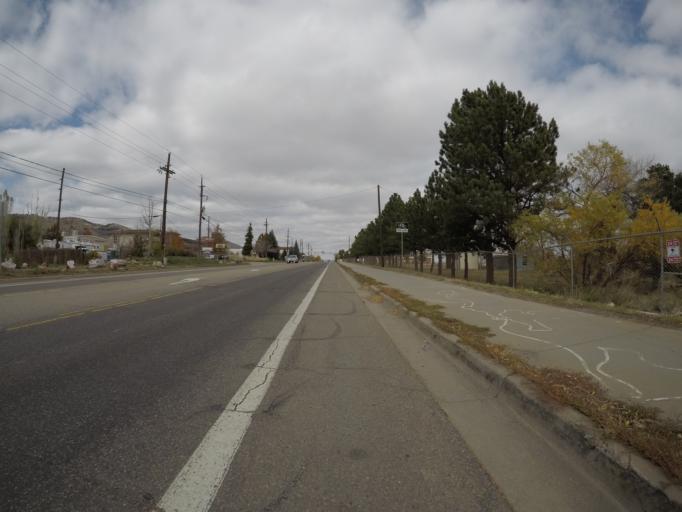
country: US
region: Colorado
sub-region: Boulder County
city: Boulder
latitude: 40.0600
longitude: -105.2821
